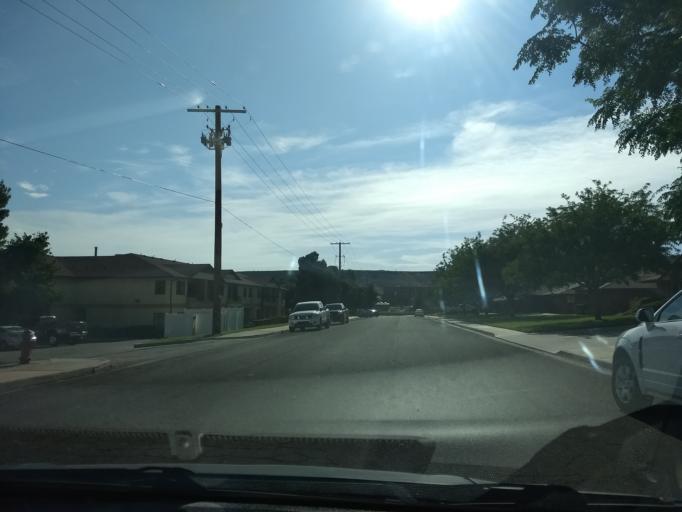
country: US
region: Utah
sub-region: Washington County
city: Saint George
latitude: 37.0923
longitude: -113.5756
